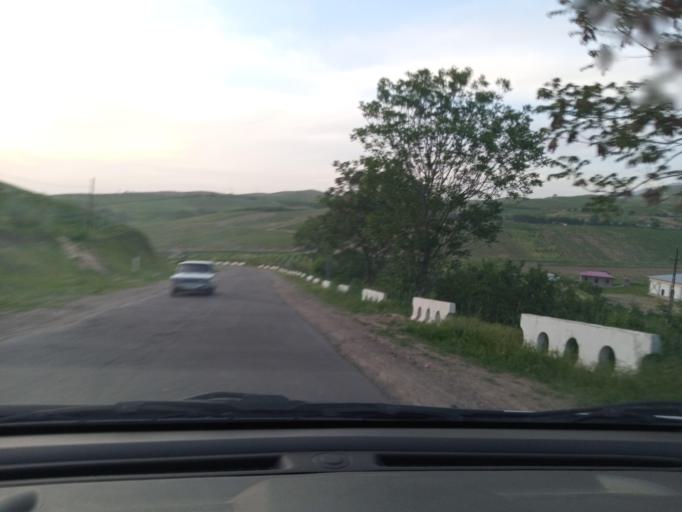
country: UZ
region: Toshkent
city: Parkent
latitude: 41.2400
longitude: 69.7330
